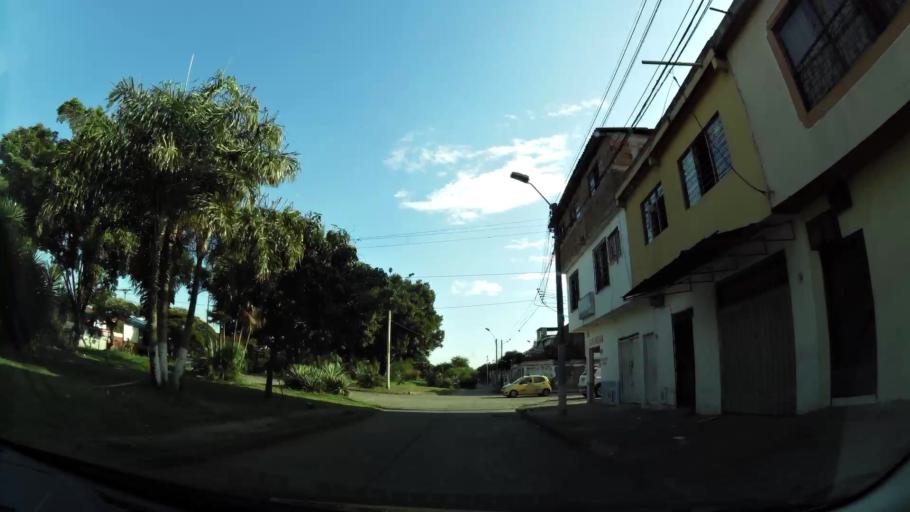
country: CO
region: Valle del Cauca
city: Cali
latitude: 3.4327
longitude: -76.5199
